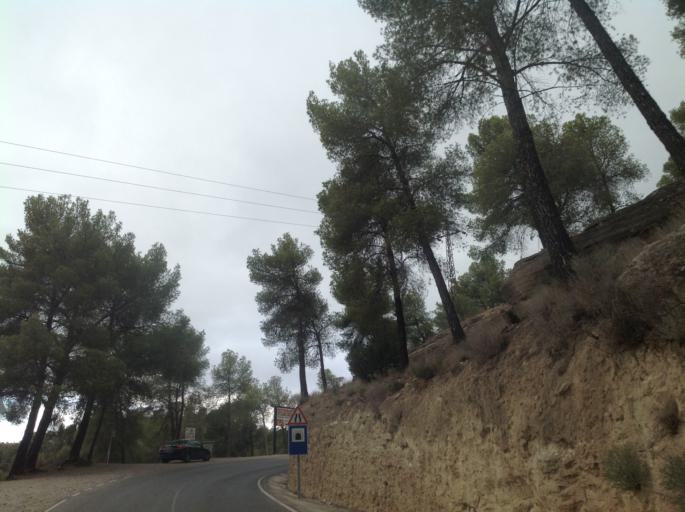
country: ES
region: Andalusia
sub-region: Provincia de Malaga
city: Ardales
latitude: 36.9269
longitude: -4.8011
